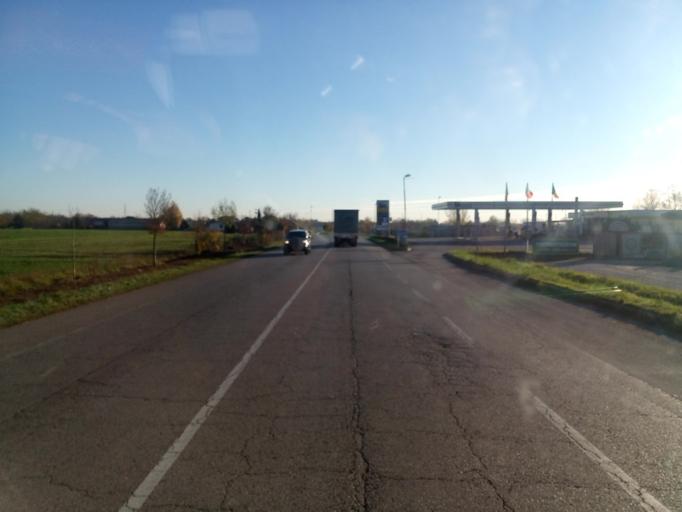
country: IT
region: Veneto
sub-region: Provincia di Vicenza
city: Sarcedo
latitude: 45.6939
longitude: 11.5083
